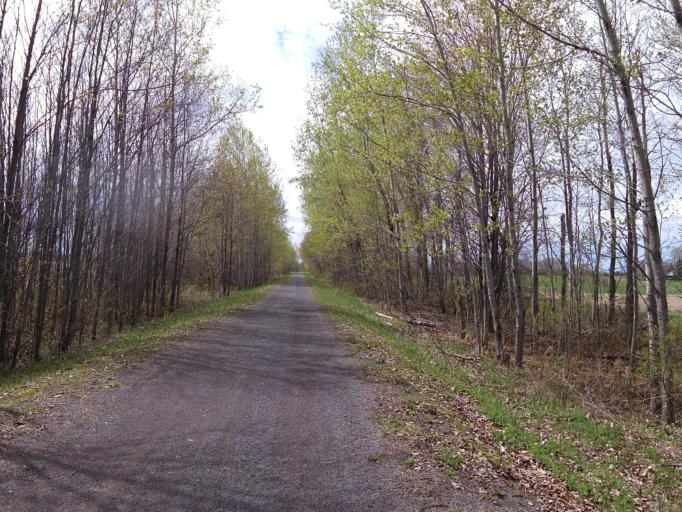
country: CA
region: Ontario
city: Hawkesbury
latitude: 45.5395
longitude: -74.7363
